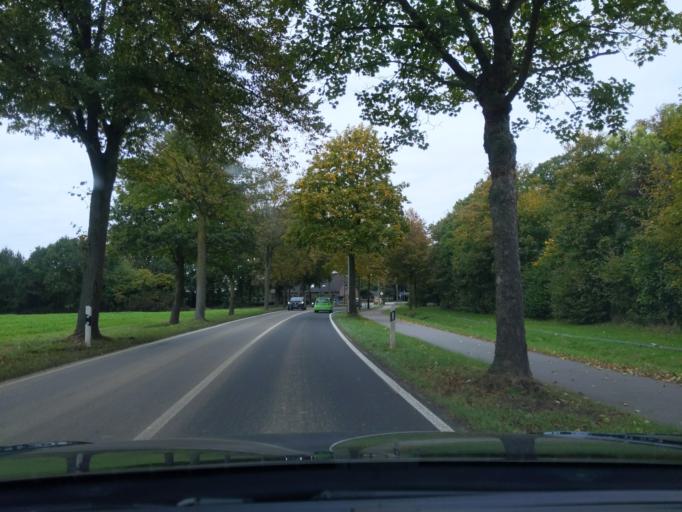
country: DE
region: North Rhine-Westphalia
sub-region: Regierungsbezirk Dusseldorf
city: Kleve
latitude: 51.8032
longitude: 6.1235
